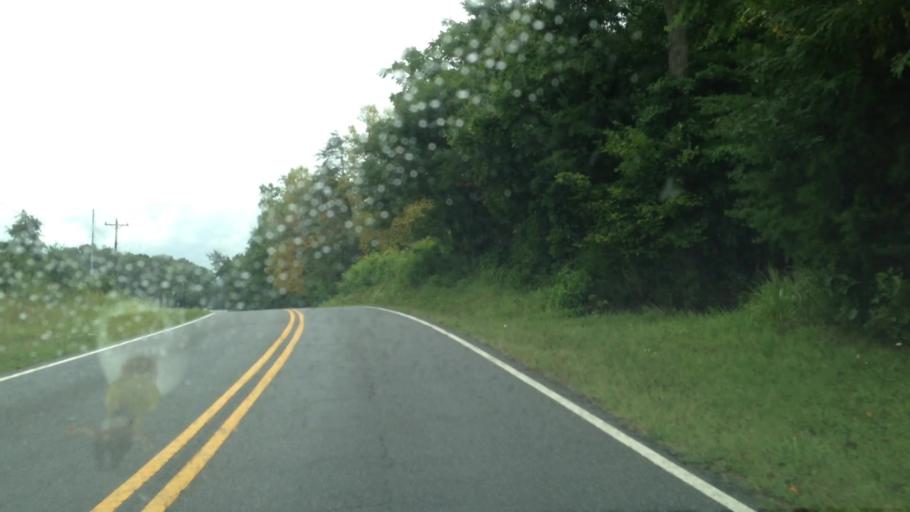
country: US
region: North Carolina
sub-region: Stokes County
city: Walnut Cove
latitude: 36.2376
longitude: -80.1074
